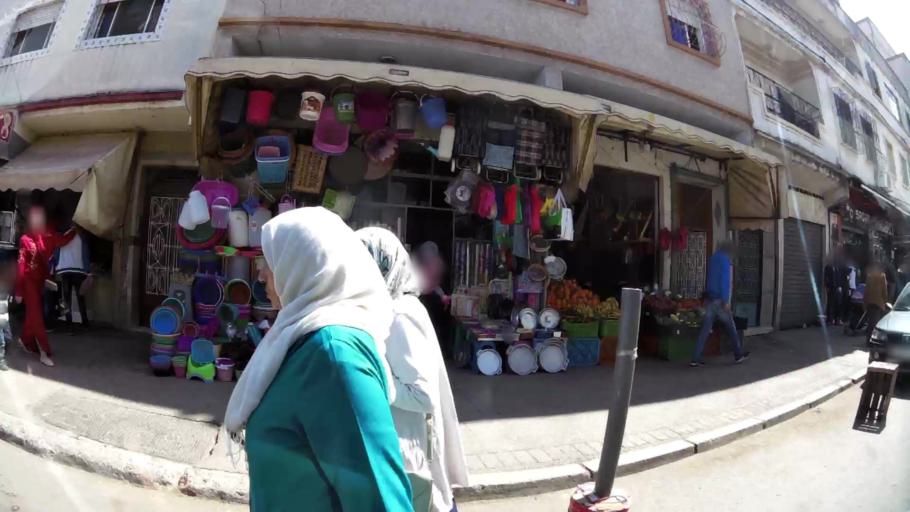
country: MA
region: Tanger-Tetouan
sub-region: Tanger-Assilah
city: Tangier
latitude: 35.7532
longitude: -5.8203
